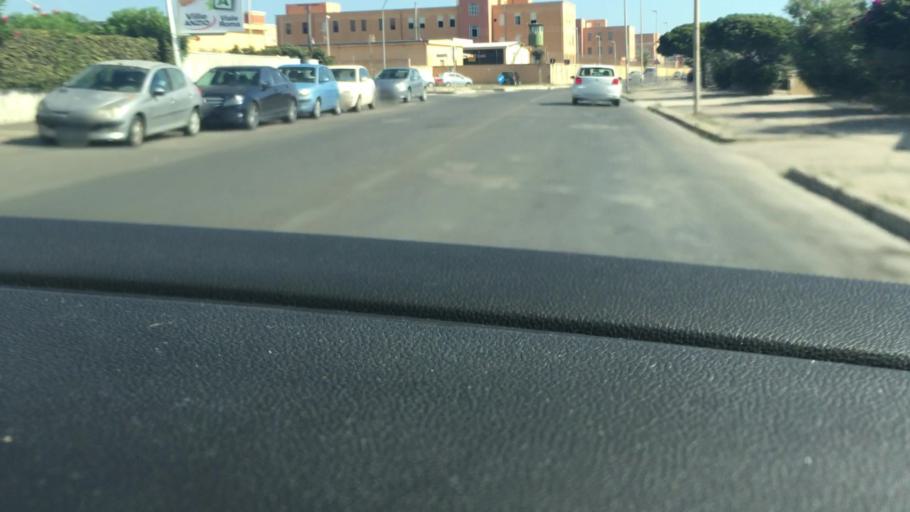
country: IT
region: Latium
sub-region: Citta metropolitana di Roma Capitale
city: Anzio
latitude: 41.4550
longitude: 12.6171
